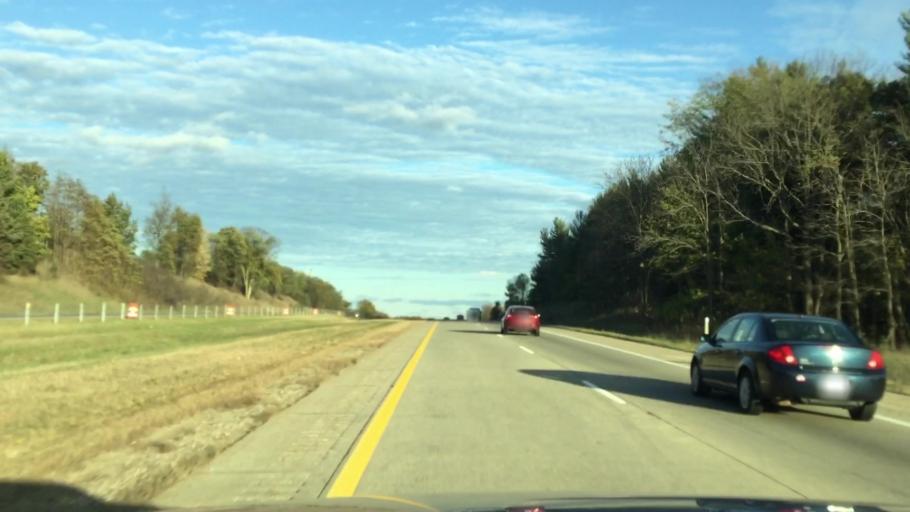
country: US
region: Michigan
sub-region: Calhoun County
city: Albion
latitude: 42.2833
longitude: -84.8394
